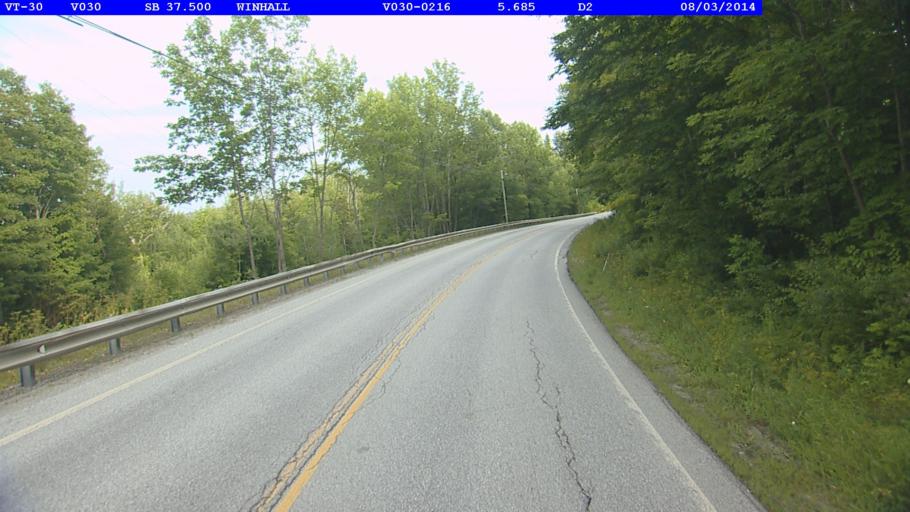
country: US
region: Vermont
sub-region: Bennington County
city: Manchester Center
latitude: 43.1882
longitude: -72.9373
